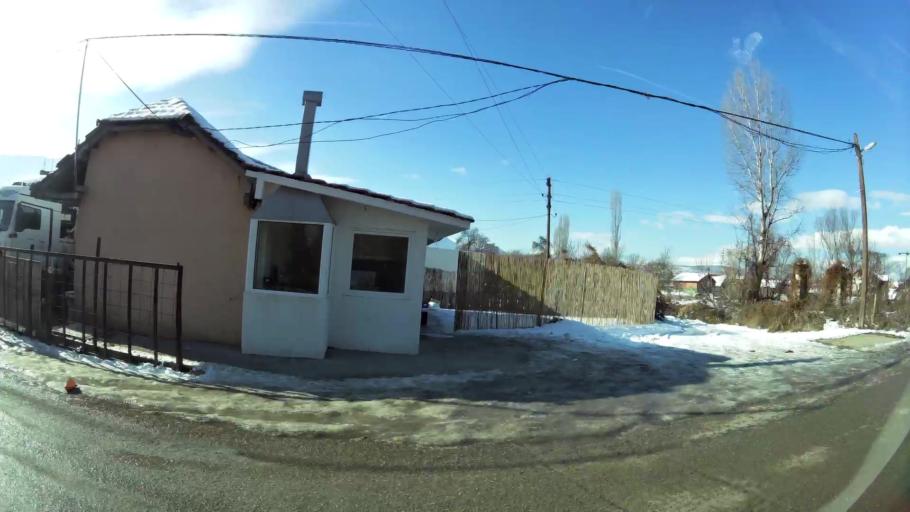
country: MK
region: Saraj
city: Saraj
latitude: 41.9984
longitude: 21.3422
